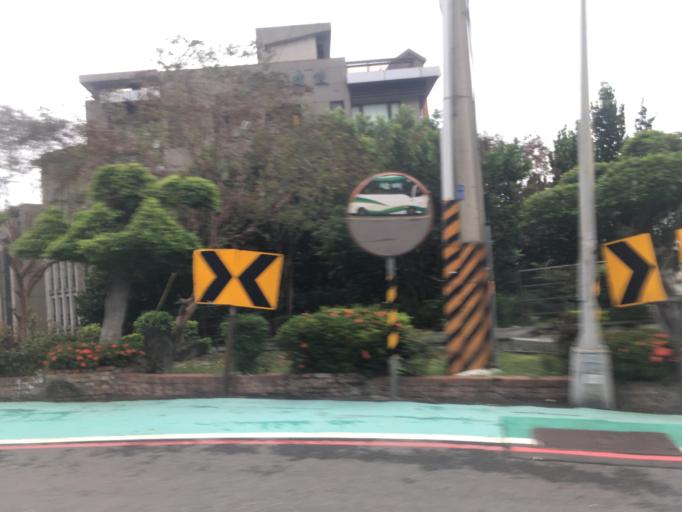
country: TW
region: Taipei
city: Taipei
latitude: 25.1276
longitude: 121.5290
